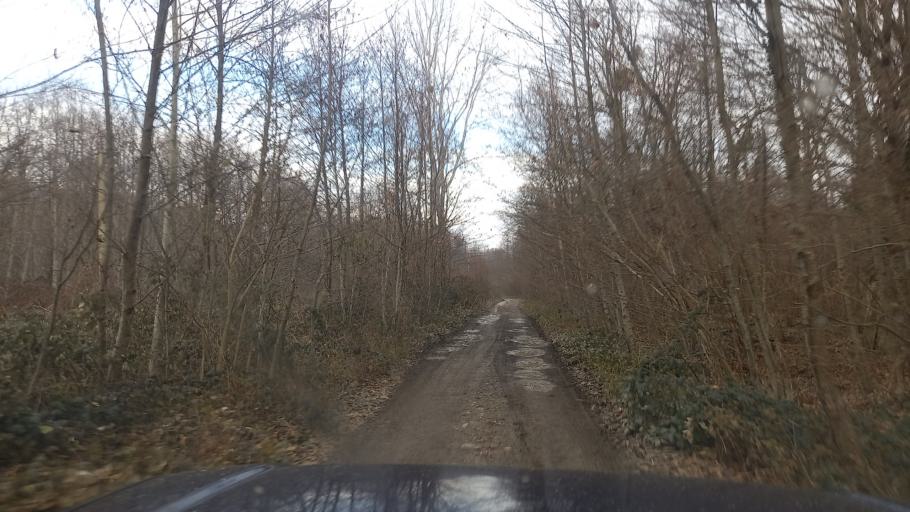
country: RU
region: Krasnodarskiy
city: Neftegorsk
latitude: 44.2219
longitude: 39.7332
